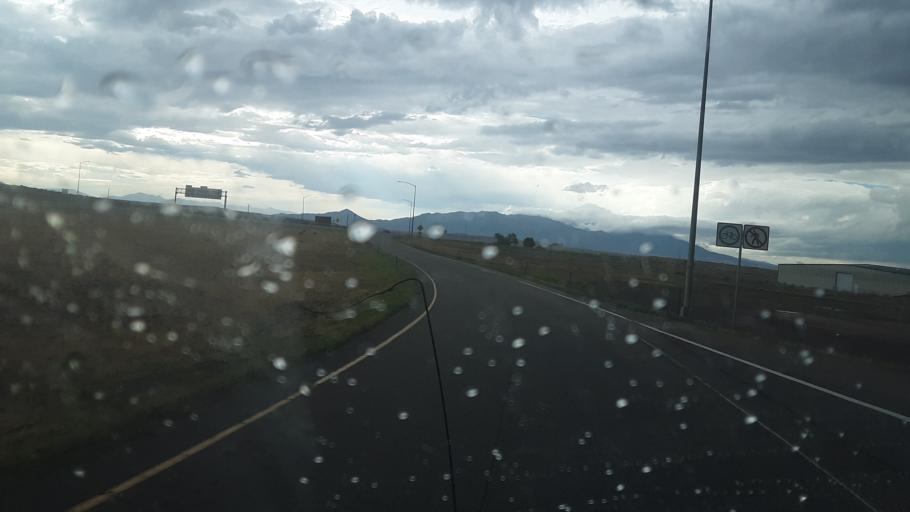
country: US
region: Colorado
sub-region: Huerfano County
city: Walsenburg
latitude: 37.6598
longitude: -104.7936
